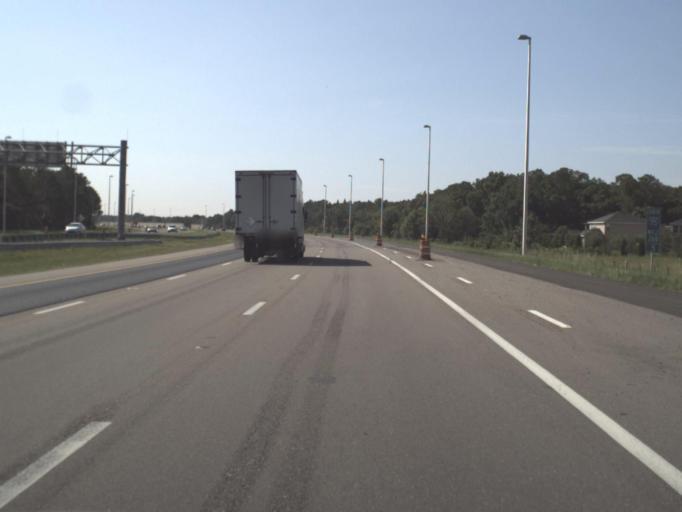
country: US
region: Florida
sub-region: Hillsborough County
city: Pebble Creek
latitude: 28.1031
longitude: -82.3676
